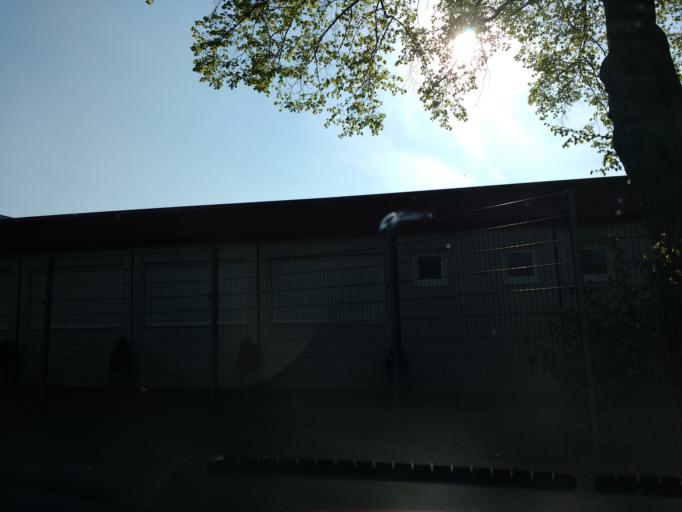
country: DE
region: North Rhine-Westphalia
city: Bad Lippspringe
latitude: 51.7657
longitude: 8.7860
